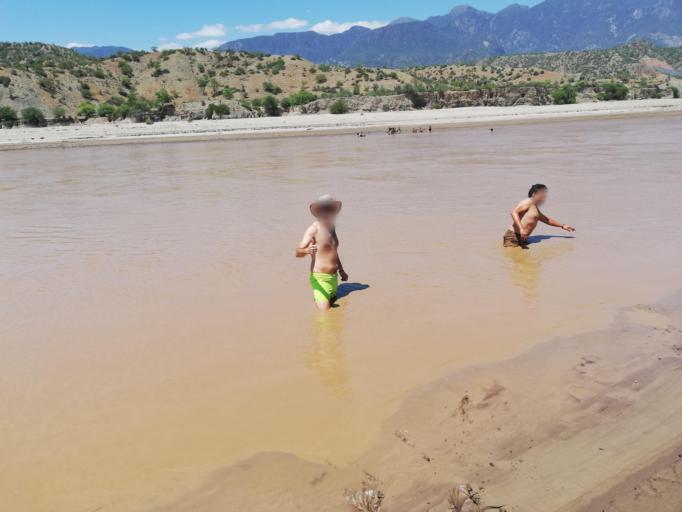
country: BO
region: Chuquisaca
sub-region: Provincia Zudanez
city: Mojocoya
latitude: -18.7072
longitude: -64.5059
